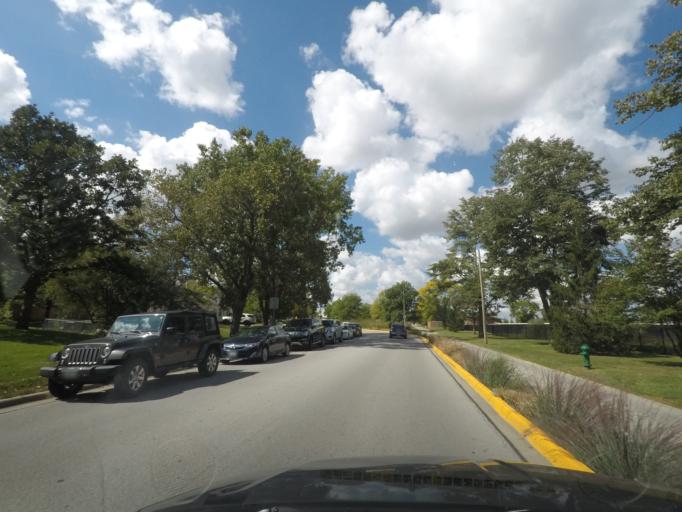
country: US
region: Iowa
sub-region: Story County
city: Ames
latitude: 42.0119
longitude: -93.6452
